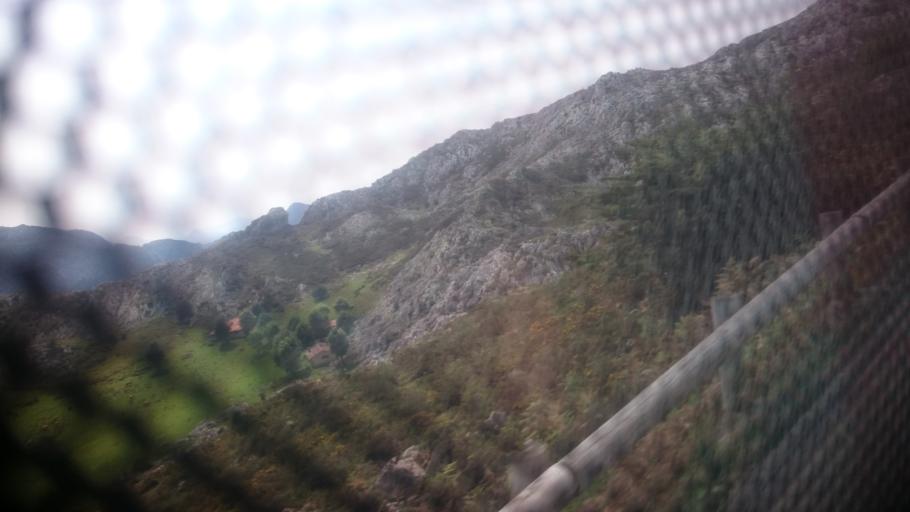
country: ES
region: Asturias
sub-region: Province of Asturias
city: Amieva
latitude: 43.2834
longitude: -5.0061
